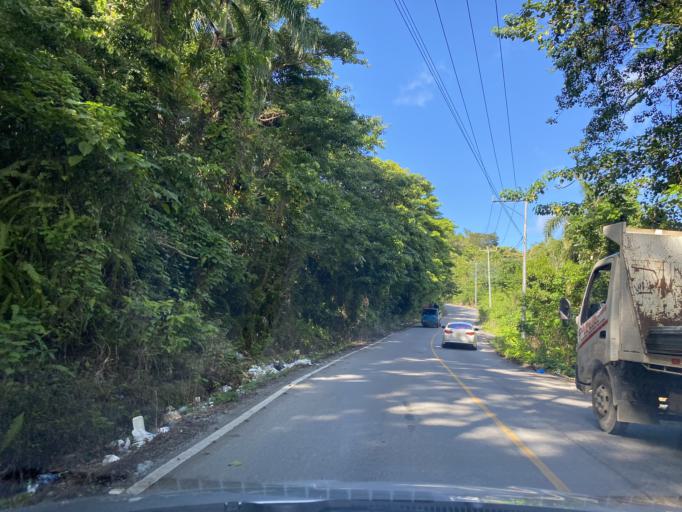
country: DO
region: Samana
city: Sanchez
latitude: 19.2391
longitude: -69.5978
